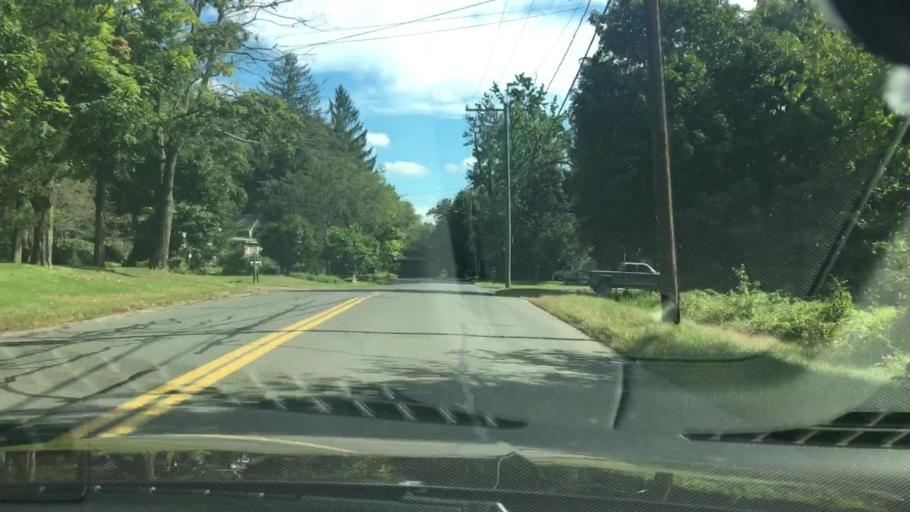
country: US
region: Connecticut
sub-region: Hartford County
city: Plainville
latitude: 41.6776
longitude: -72.8810
